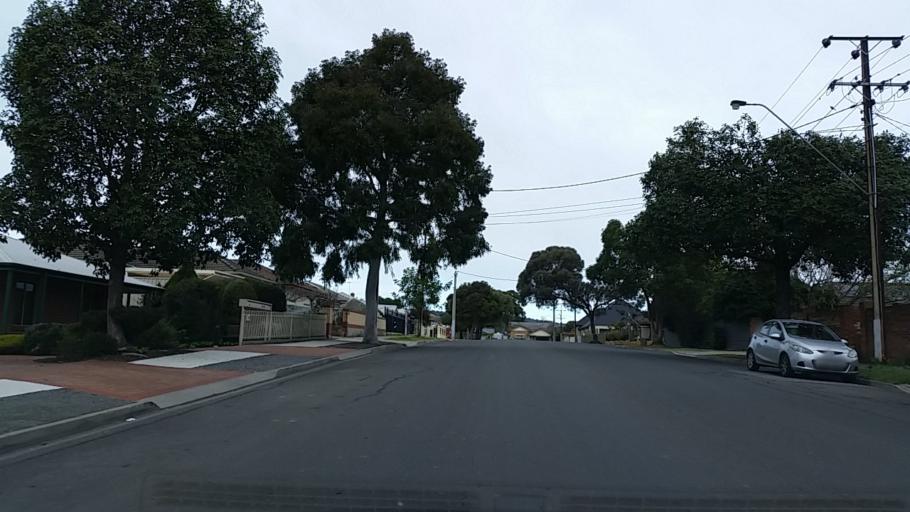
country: AU
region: South Australia
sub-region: Campbelltown
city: Hectorville
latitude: -34.9044
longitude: 138.6541
